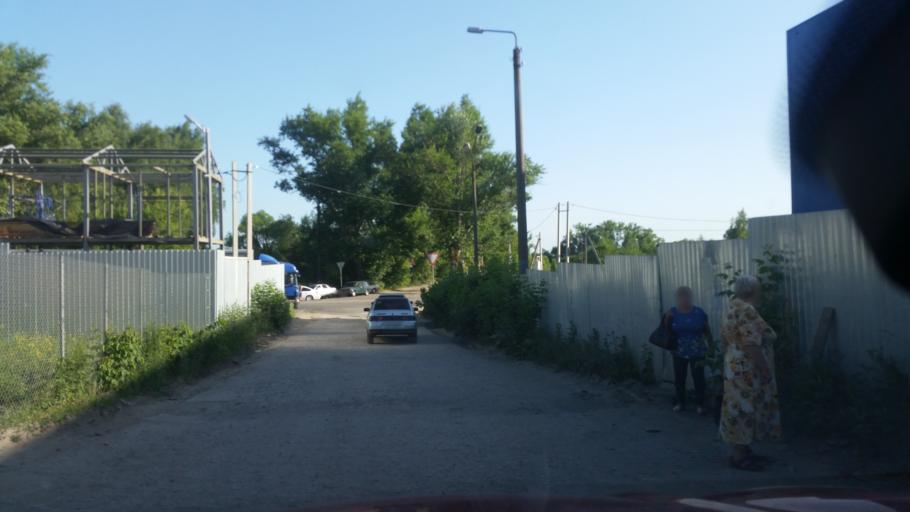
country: RU
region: Orjol
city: Znamenka
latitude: 52.9189
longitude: 35.9866
